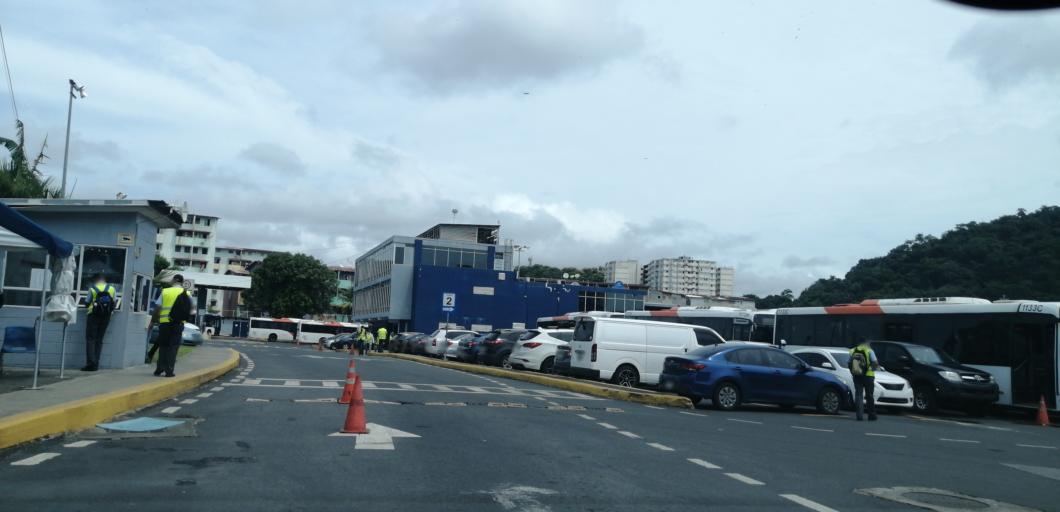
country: PA
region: Panama
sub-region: Distrito de Panama
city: Ancon
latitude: 8.9488
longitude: -79.5438
